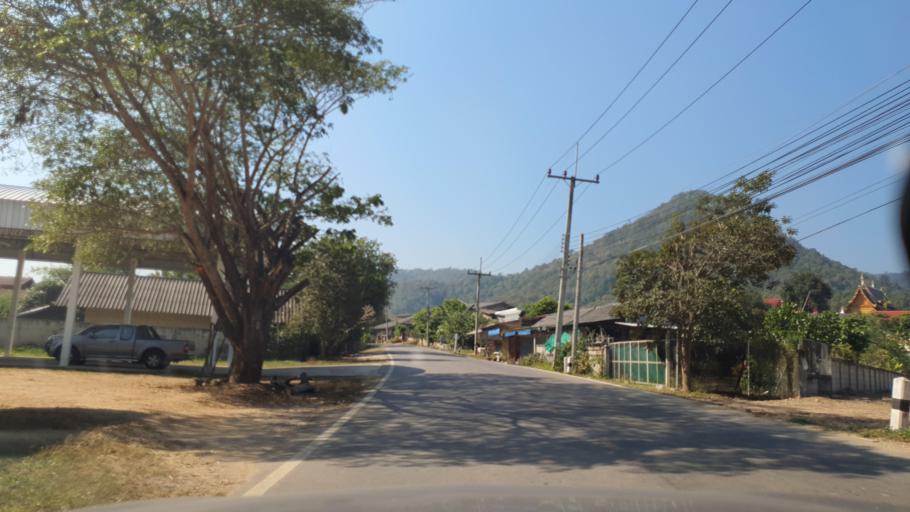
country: TH
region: Lamphun
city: Ban Thi
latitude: 18.5873
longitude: 99.2639
